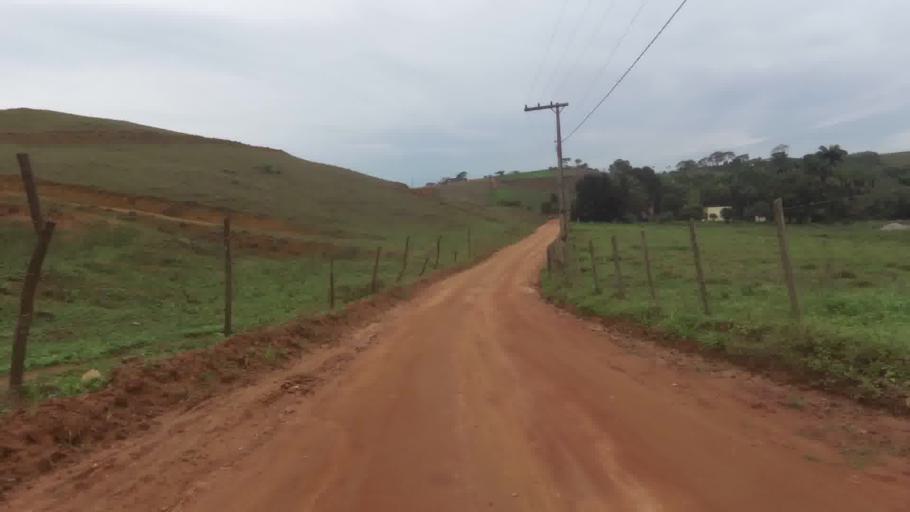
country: BR
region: Espirito Santo
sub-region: Iconha
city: Iconha
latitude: -20.8004
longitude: -40.8170
